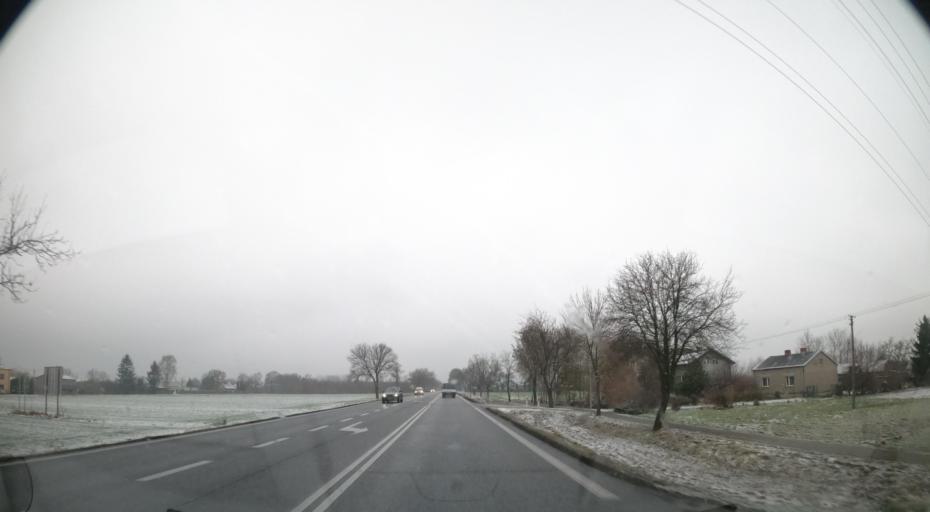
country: PL
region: Masovian Voivodeship
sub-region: Powiat sochaczewski
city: Teresin
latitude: 52.2164
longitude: 20.3820
